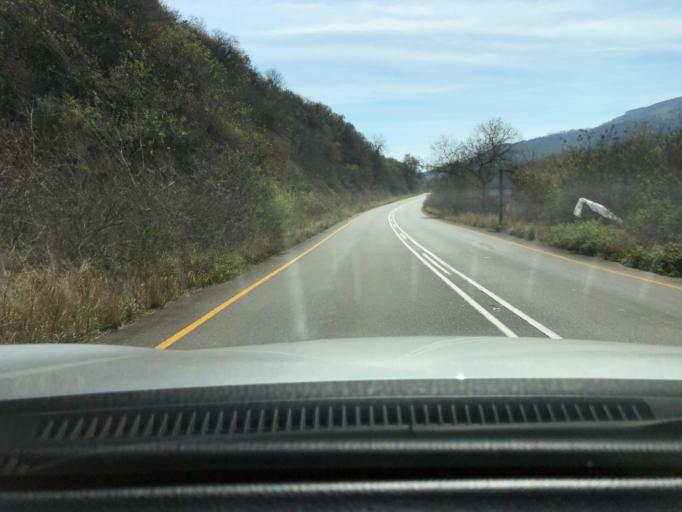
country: ZA
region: KwaZulu-Natal
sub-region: uMgungundlovu District Municipality
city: Richmond
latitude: -29.9769
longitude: 30.2505
